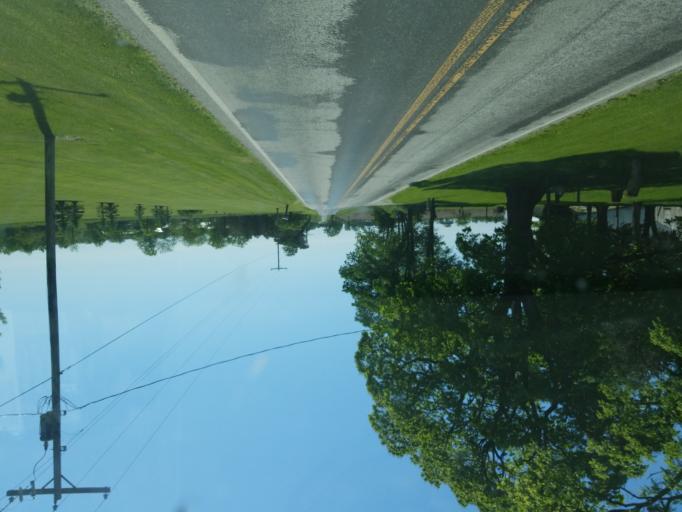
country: US
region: Ohio
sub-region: Hardin County
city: Kenton
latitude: 40.6219
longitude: -83.4520
